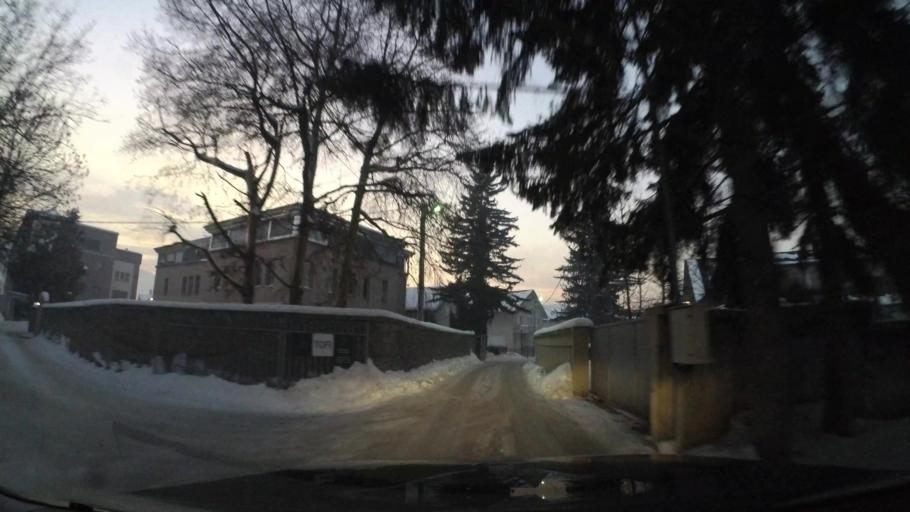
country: BA
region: Federation of Bosnia and Herzegovina
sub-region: Kanton Sarajevo
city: Sarajevo
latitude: 43.8356
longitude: 18.3209
